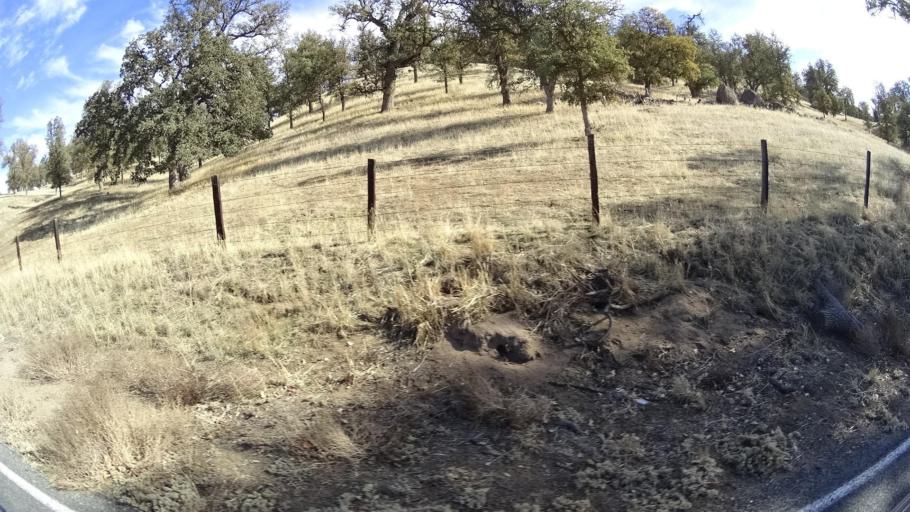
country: US
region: California
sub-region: Kern County
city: Alta Sierra
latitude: 35.7129
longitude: -118.7275
